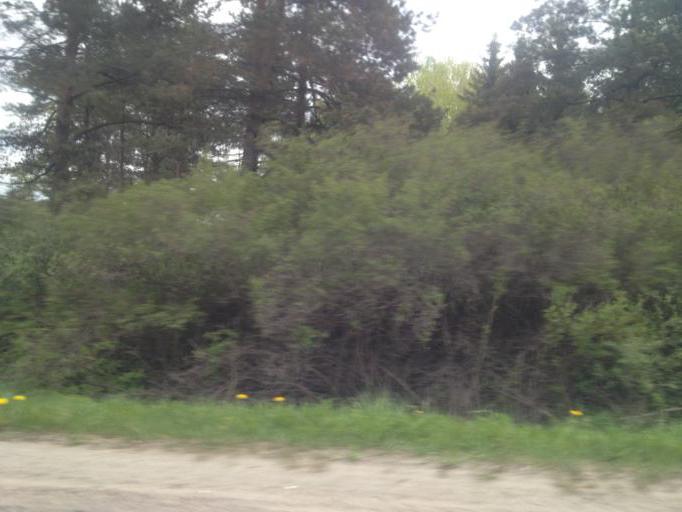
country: FI
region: Uusimaa
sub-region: Helsinki
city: Helsinki
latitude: 60.2348
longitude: 24.9005
